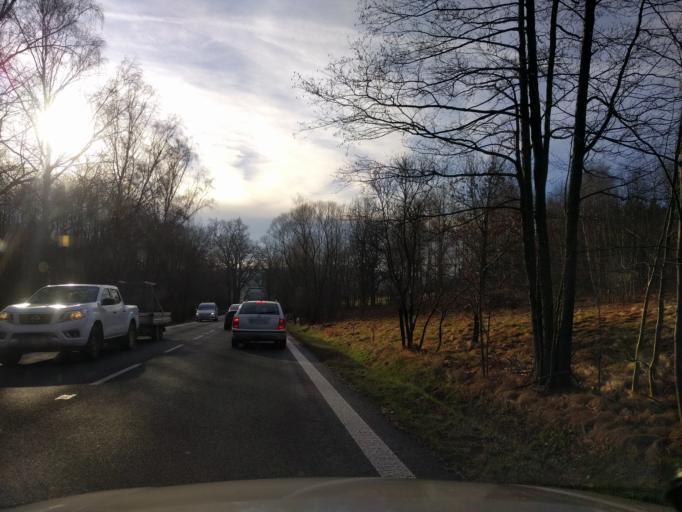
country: CZ
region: Liberecky
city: Mnisek
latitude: 50.8508
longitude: 15.0312
